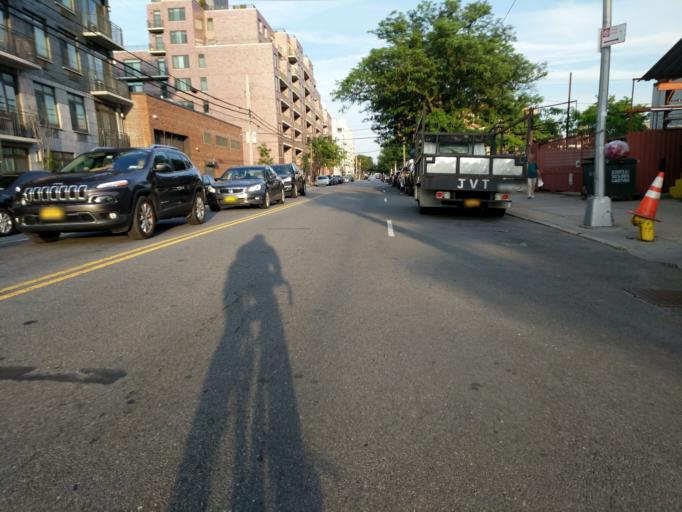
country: US
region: New York
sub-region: Queens County
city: Long Island City
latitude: 40.7674
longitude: -73.9357
